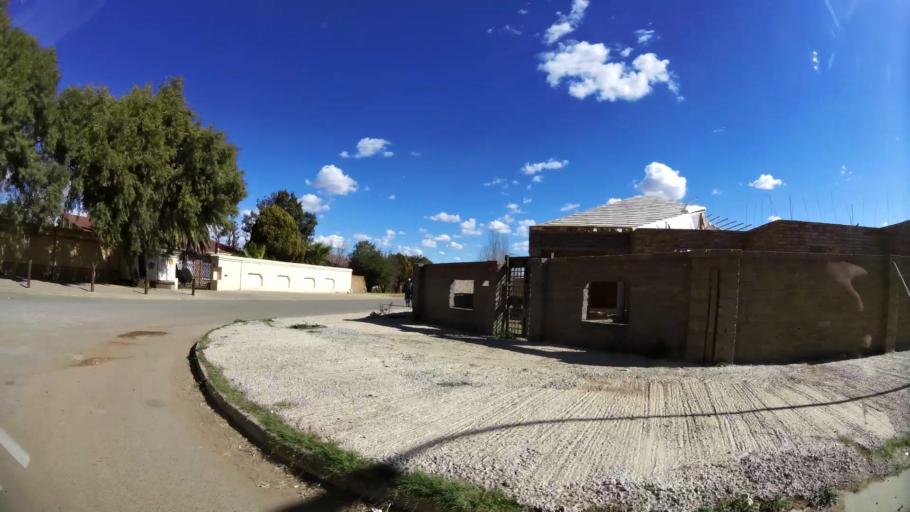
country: ZA
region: North-West
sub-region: Dr Kenneth Kaunda District Municipality
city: Klerksdorp
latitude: -26.8751
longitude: 26.5834
